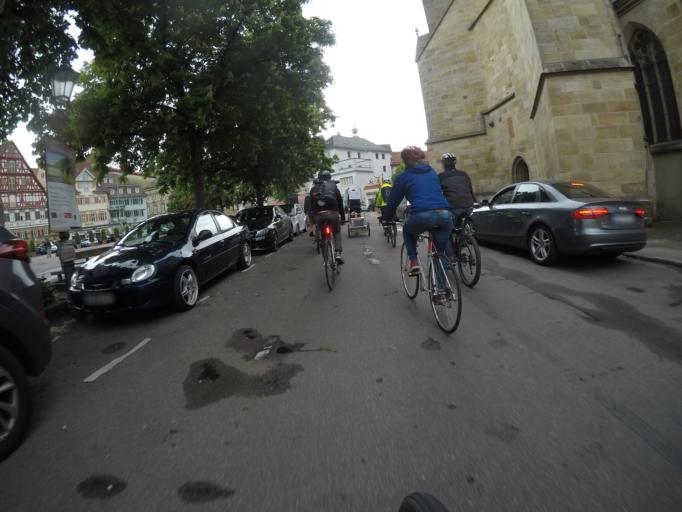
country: DE
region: Baden-Wuerttemberg
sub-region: Regierungsbezirk Stuttgart
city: Esslingen
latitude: 48.7425
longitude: 9.3062
